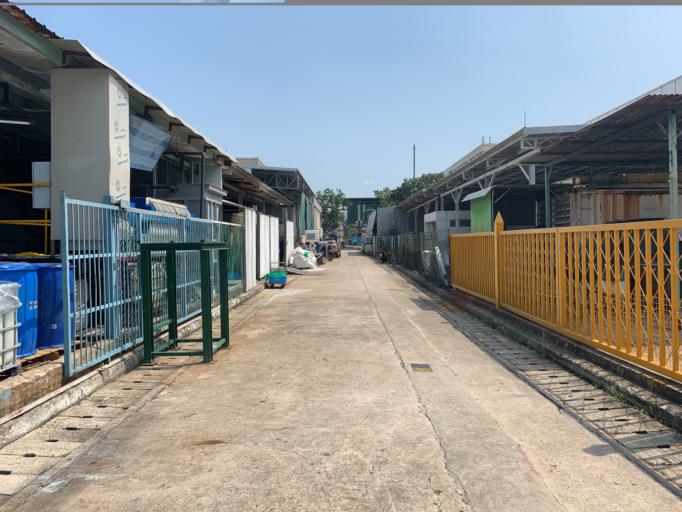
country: MY
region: Johor
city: Johor Bahru
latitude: 1.3072
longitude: 103.6294
